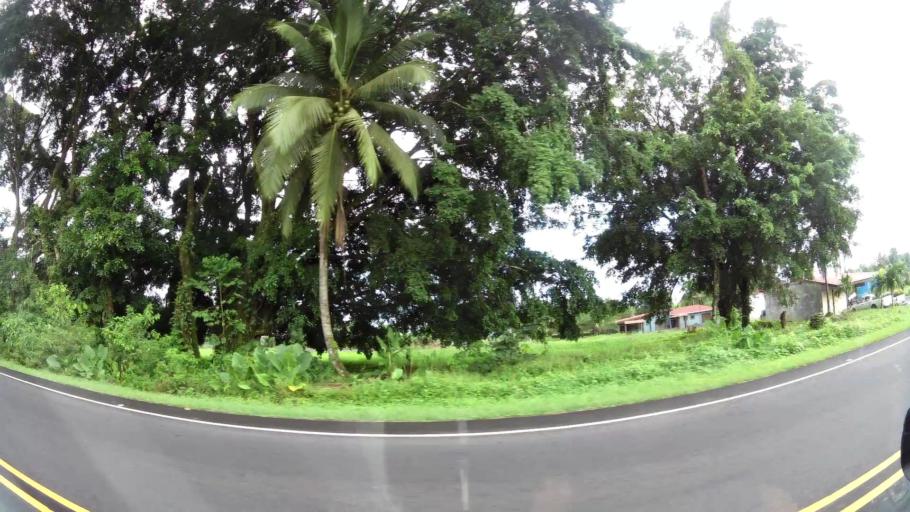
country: CR
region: Limon
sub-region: Canton de Guacimo
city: Guacimo
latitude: 10.2091
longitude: -83.6969
